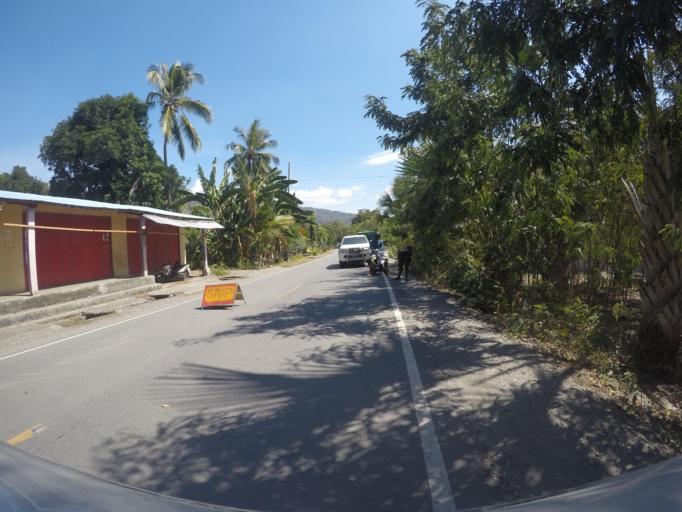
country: TL
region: Liquica
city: Liquica
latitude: -8.5867
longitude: 125.3495
